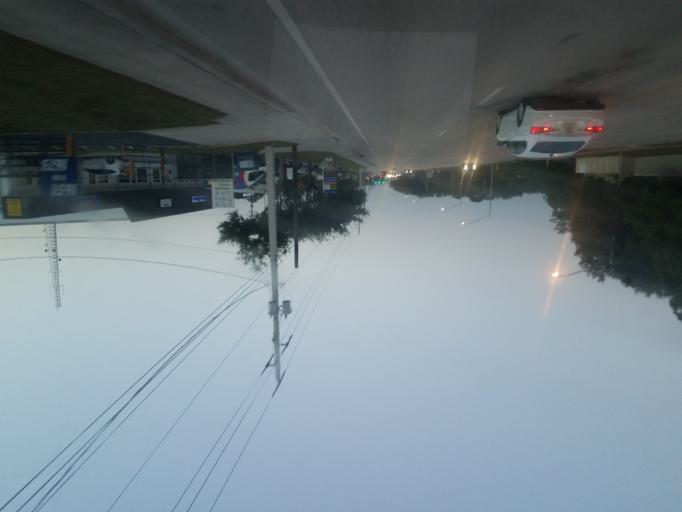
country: US
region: Florida
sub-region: Sarasota County
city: Fruitville
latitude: 27.3189
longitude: -82.4514
